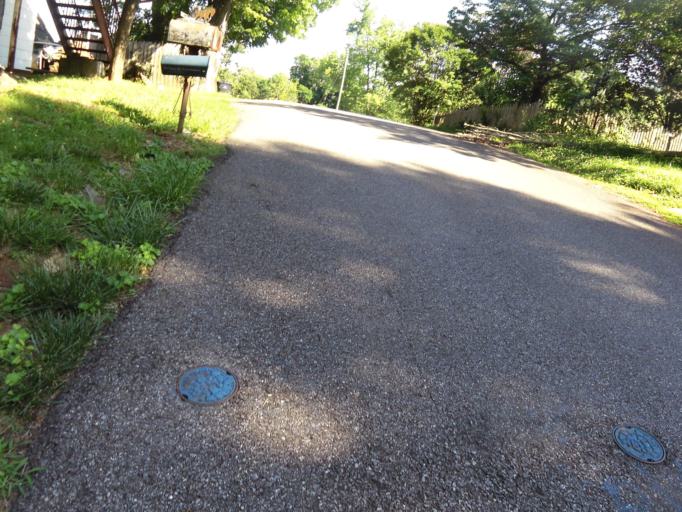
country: US
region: Tennessee
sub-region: Knox County
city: Knoxville
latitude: 35.9535
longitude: -83.9068
